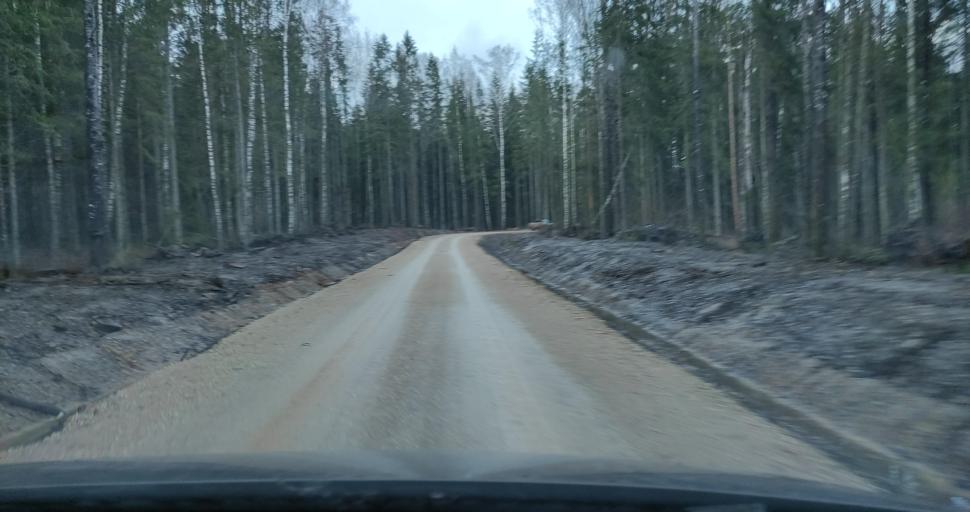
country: LV
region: Skrunda
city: Skrunda
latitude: 56.7417
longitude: 22.1914
